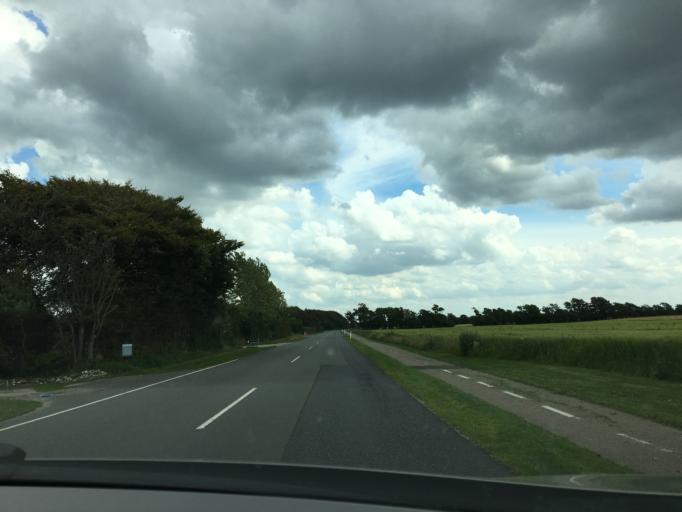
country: DK
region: Central Jutland
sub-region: Ringkobing-Skjern Kommune
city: Skjern
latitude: 55.9524
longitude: 8.4032
